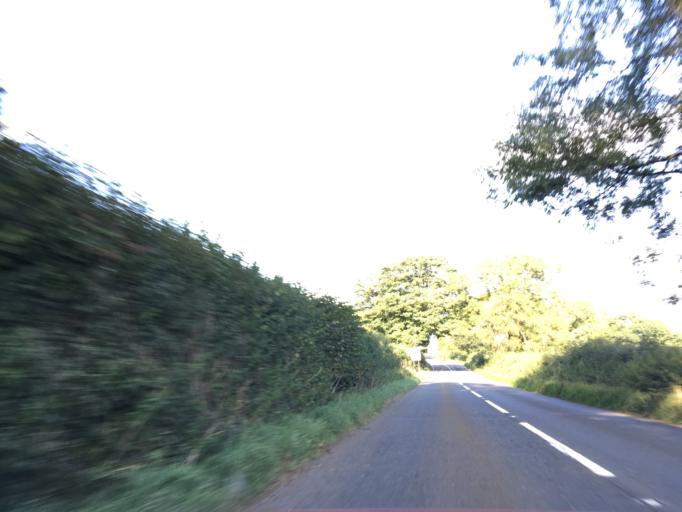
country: GB
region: England
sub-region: Somerset
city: Chilcompton
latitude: 51.2567
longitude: -2.5566
